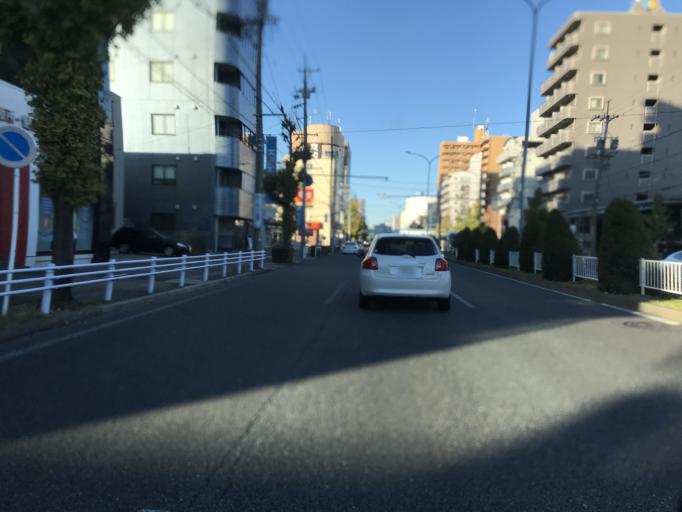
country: JP
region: Aichi
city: Nagoya-shi
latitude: 35.1643
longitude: 136.8717
